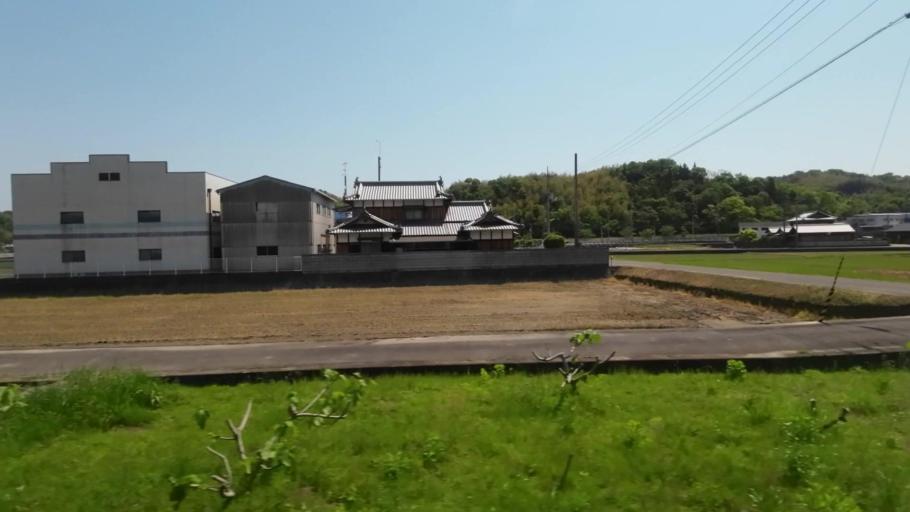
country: JP
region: Ehime
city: Saijo
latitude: 34.0042
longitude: 133.0363
